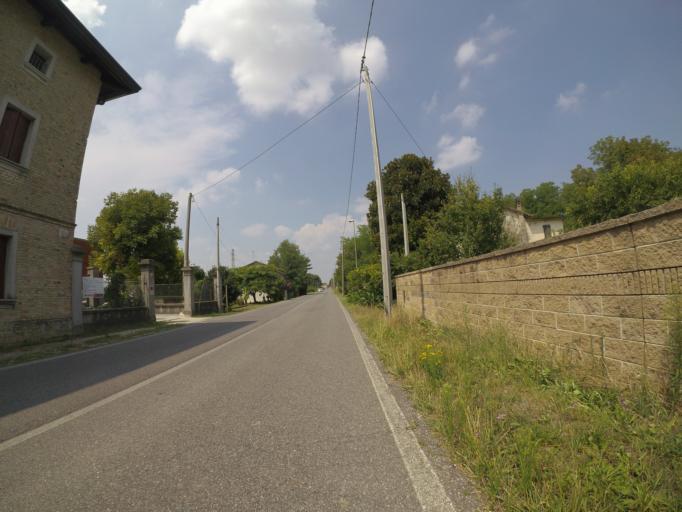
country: IT
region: Friuli Venezia Giulia
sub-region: Provincia di Udine
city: Teor
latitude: 45.8456
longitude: 13.0748
